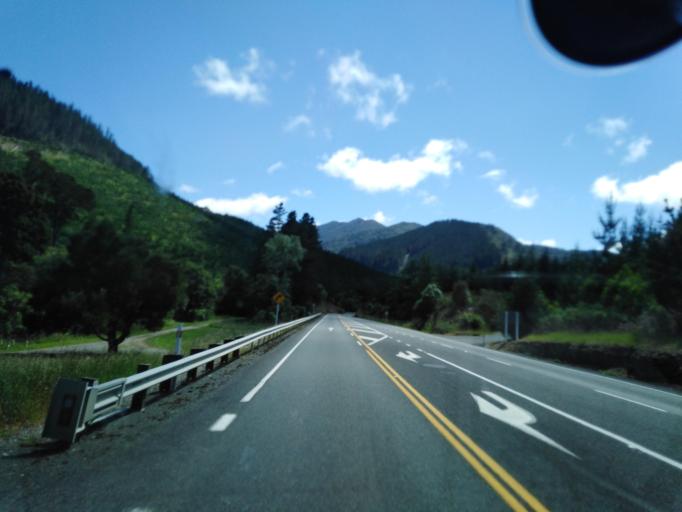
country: NZ
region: Nelson
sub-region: Nelson City
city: Nelson
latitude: -41.1787
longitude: 173.5601
